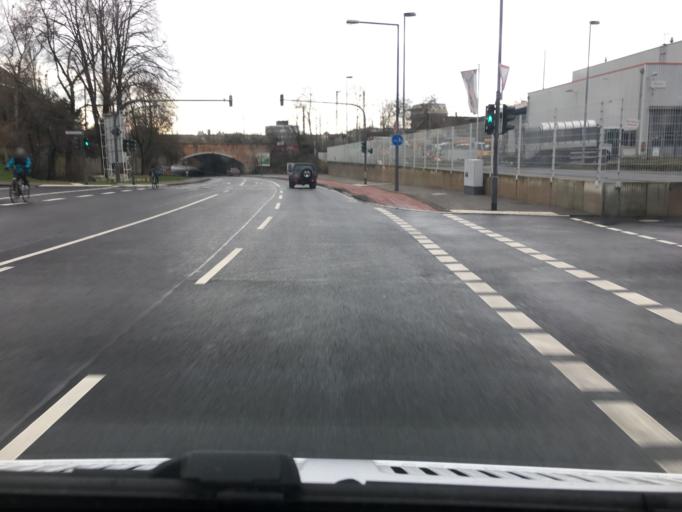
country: DE
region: North Rhine-Westphalia
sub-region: Regierungsbezirk Koln
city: Bilderstoeckchen
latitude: 50.9511
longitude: 6.8979
